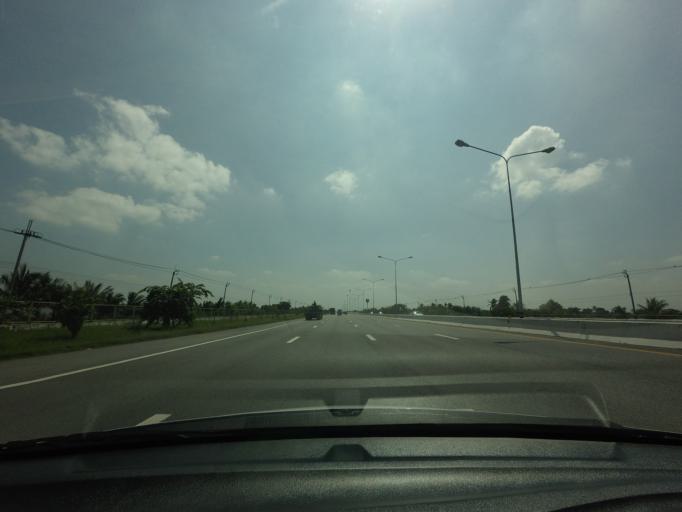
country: TH
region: Samut Prakan
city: Ban Khlong Bang Sao Thong
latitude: 13.6324
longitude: 100.9025
